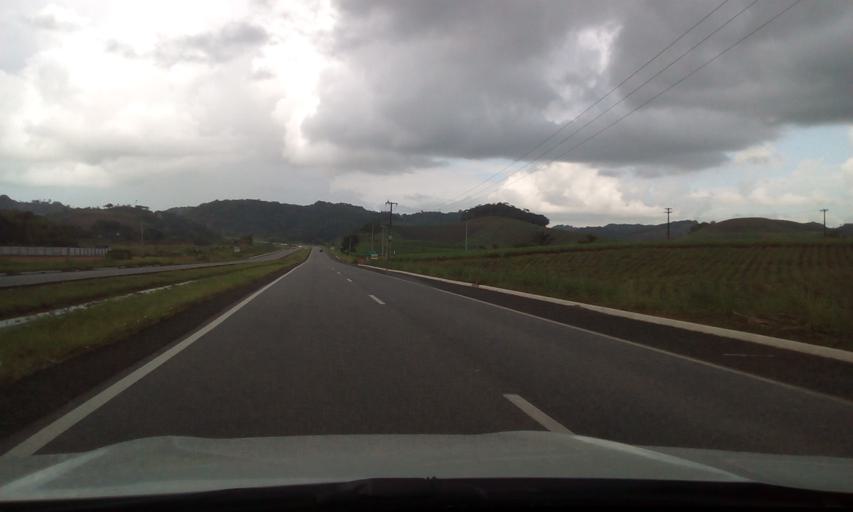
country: BR
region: Pernambuco
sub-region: Cabo De Santo Agostinho
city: Cabo
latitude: -8.2557
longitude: -35.0363
